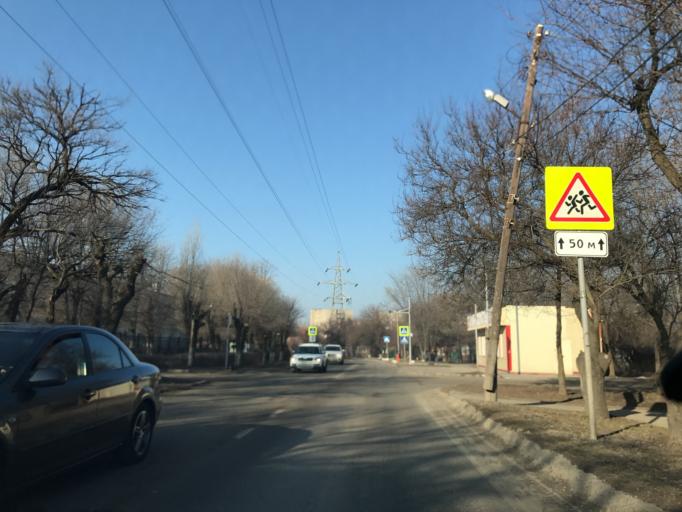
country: RU
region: Rostov
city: Rostov-na-Donu
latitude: 47.2156
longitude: 39.6417
